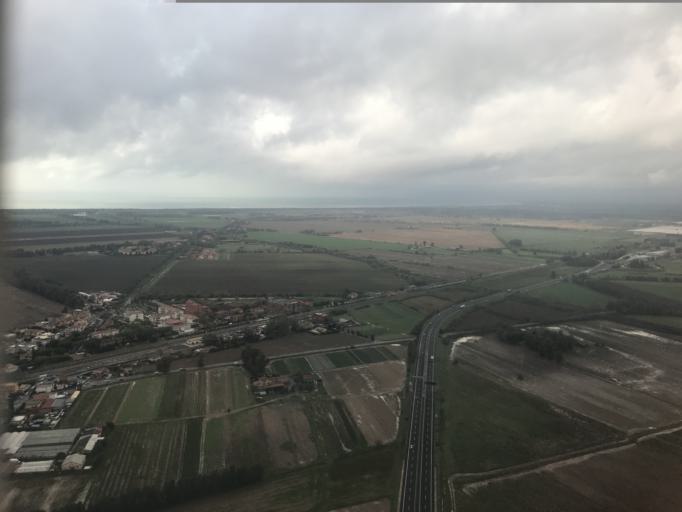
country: IT
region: Latium
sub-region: Citta metropolitana di Roma Capitale
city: Maccarese
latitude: 41.8796
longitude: 12.2479
